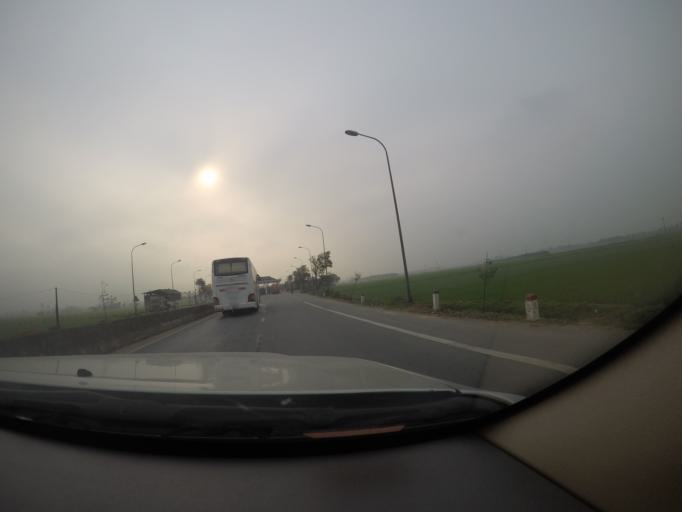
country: VN
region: Ha Tinh
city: Cam Xuyen
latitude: 18.2122
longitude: 106.1078
